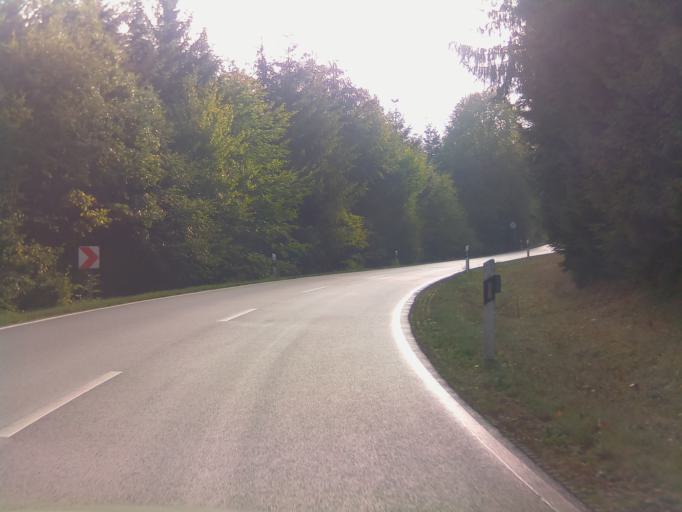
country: DE
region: Hesse
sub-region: Regierungsbezirk Kassel
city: Hosenfeld
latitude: 50.5057
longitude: 9.5352
